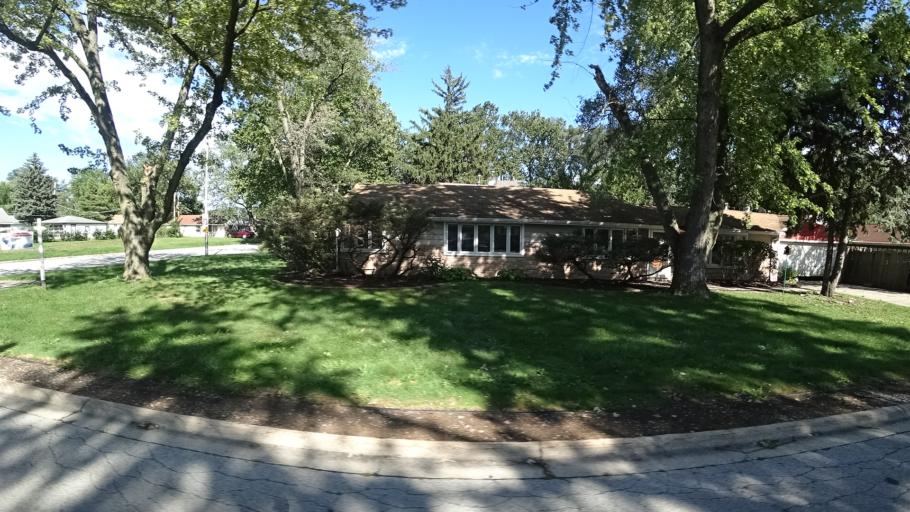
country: US
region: Illinois
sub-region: Cook County
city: Oak Lawn
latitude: 41.7104
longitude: -87.7502
